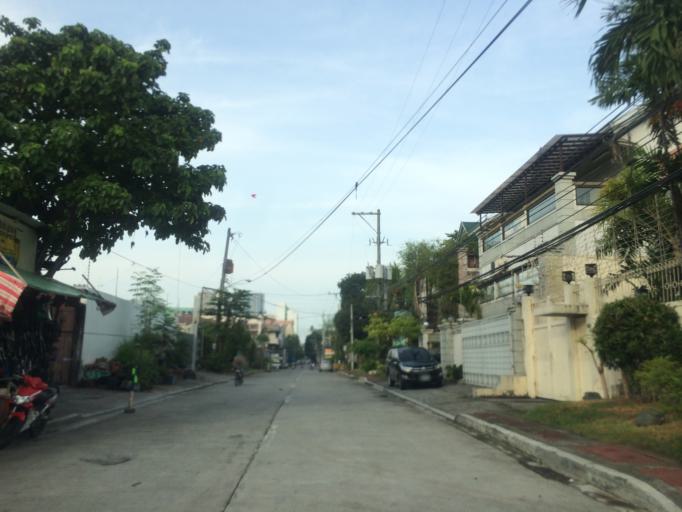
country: PH
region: Calabarzon
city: Del Monte
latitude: 14.6261
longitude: 121.0076
